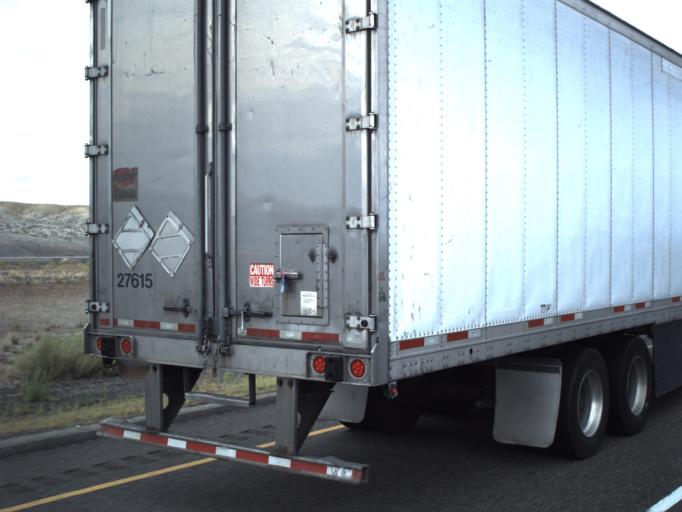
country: US
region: Utah
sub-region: Grand County
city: Moab
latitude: 38.9340
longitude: -109.4188
